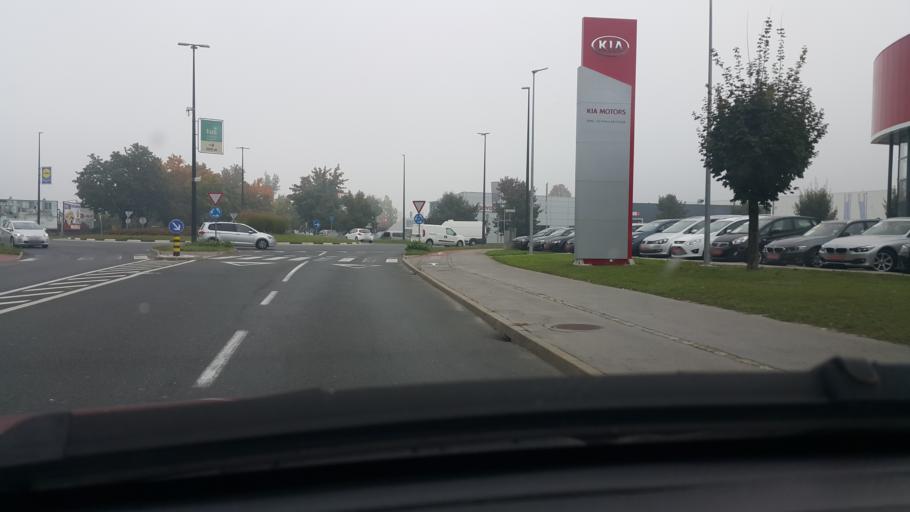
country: SI
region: Ljubljana
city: Ljubljana
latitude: 46.0664
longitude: 14.5514
